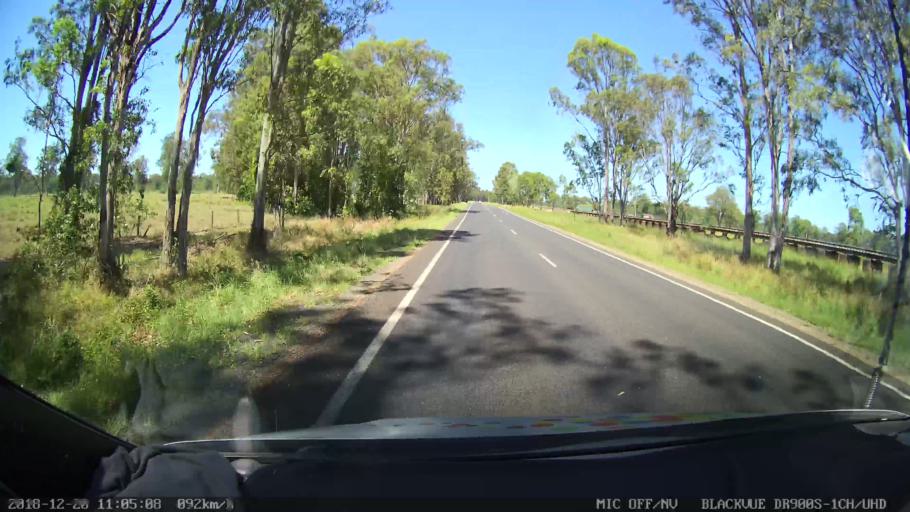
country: AU
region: New South Wales
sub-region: Richmond Valley
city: Casino
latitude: -28.8929
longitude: 153.0433
